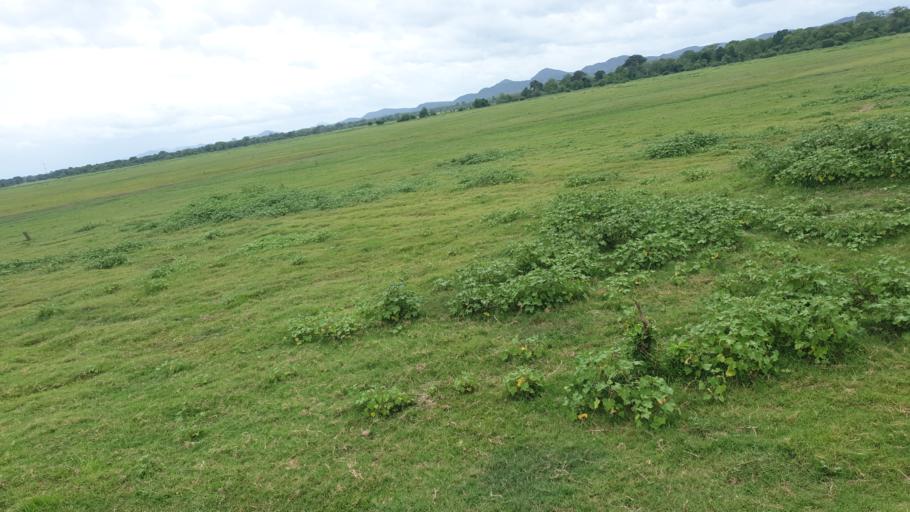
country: LK
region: North Central
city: Polonnaruwa
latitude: 8.1298
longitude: 80.9069
